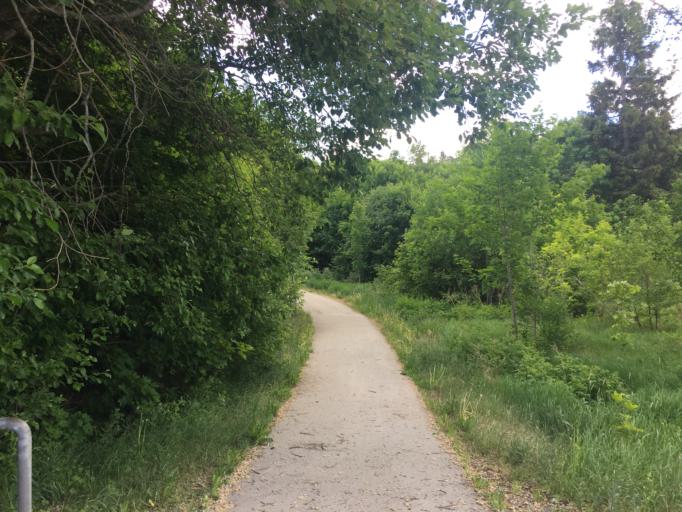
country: SE
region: Stockholm
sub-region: Norrtalje Kommun
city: Rimbo
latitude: 59.6573
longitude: 18.2686
